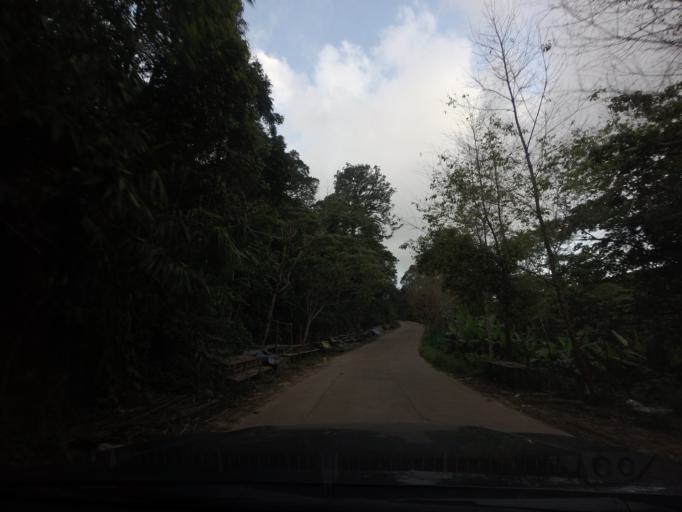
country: TH
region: Phetchabun
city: Lom Kao
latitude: 16.8991
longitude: 101.1044
